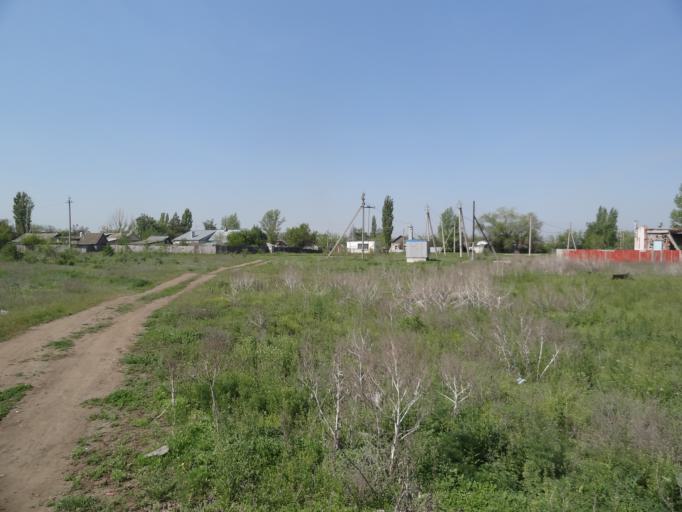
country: RU
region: Saratov
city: Privolzhskiy
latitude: 51.4137
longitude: 46.1024
